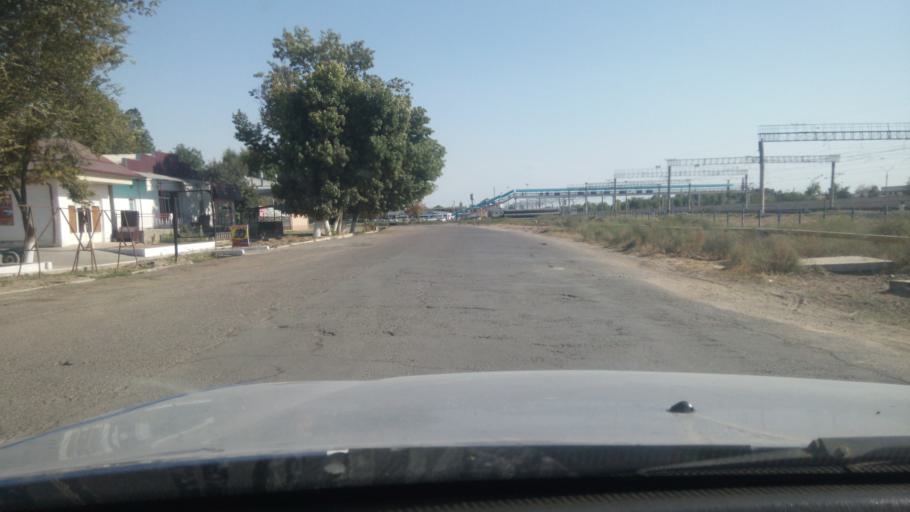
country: UZ
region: Sirdaryo
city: Guliston
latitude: 40.5008
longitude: 68.7639
